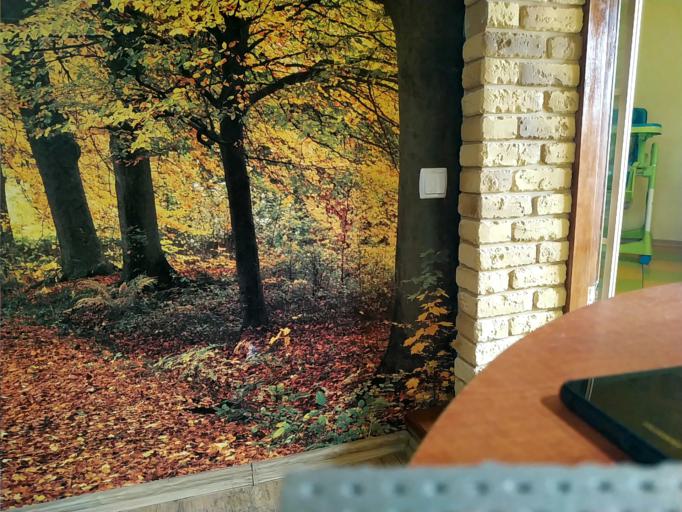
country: RU
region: Tverskaya
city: Kalashnikovo
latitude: 57.3025
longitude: 35.1073
